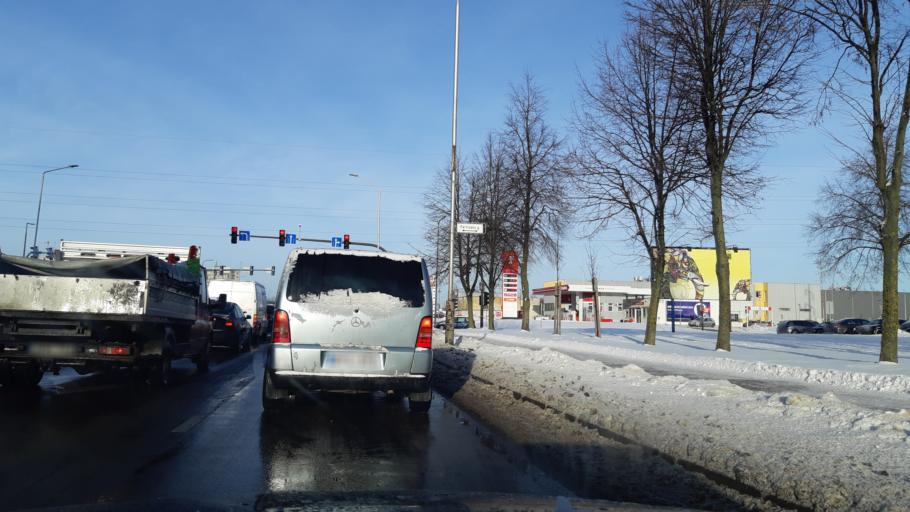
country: LT
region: Kauno apskritis
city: Dainava (Kaunas)
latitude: 54.9261
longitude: 23.9753
